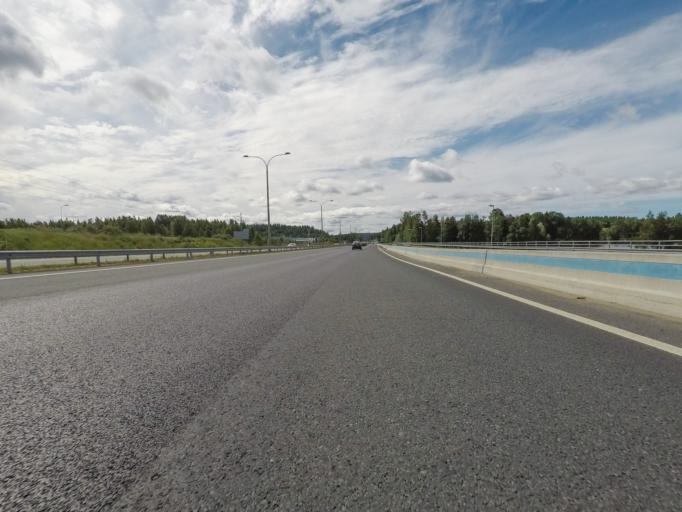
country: FI
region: Northern Savo
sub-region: Kuopio
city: Kuopio
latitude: 62.9684
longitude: 27.7028
